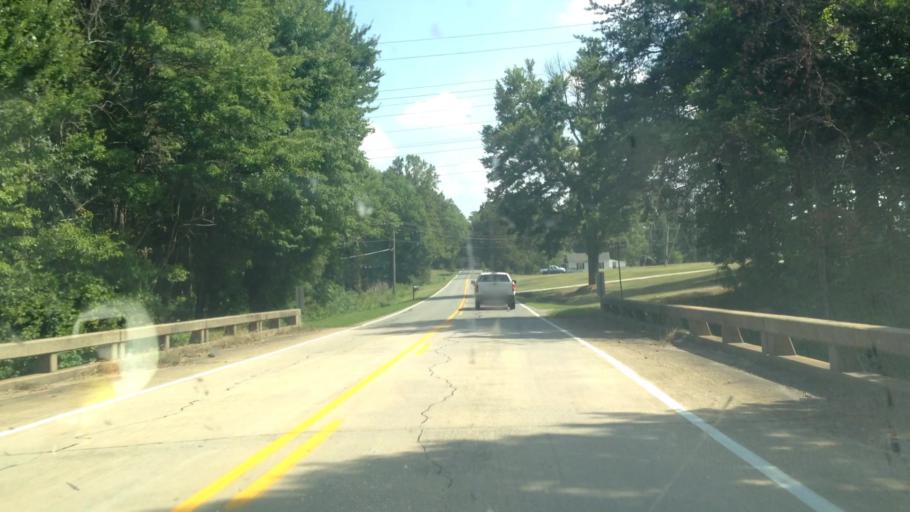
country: US
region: North Carolina
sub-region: Stokes County
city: Walnut Cove
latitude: 36.2749
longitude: -80.0883
